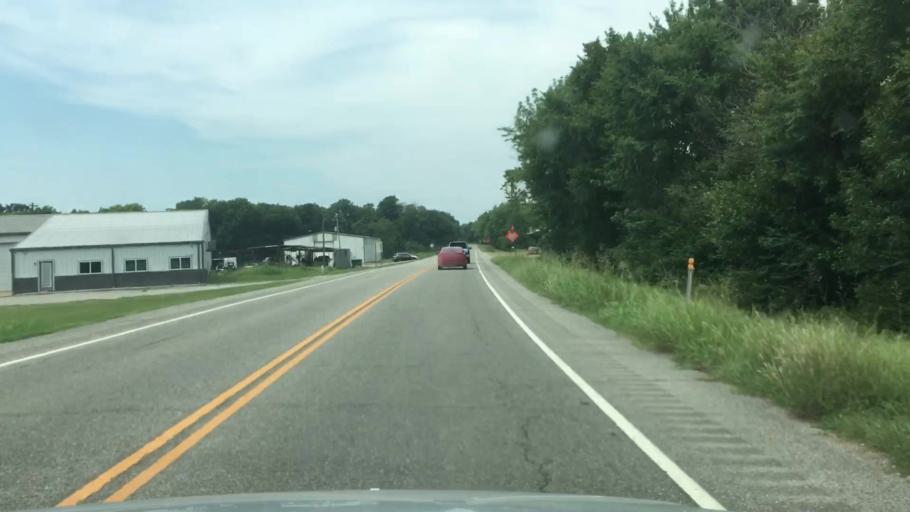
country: US
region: Oklahoma
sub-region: Muskogee County
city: Fort Gibson
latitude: 35.9341
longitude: -95.1575
